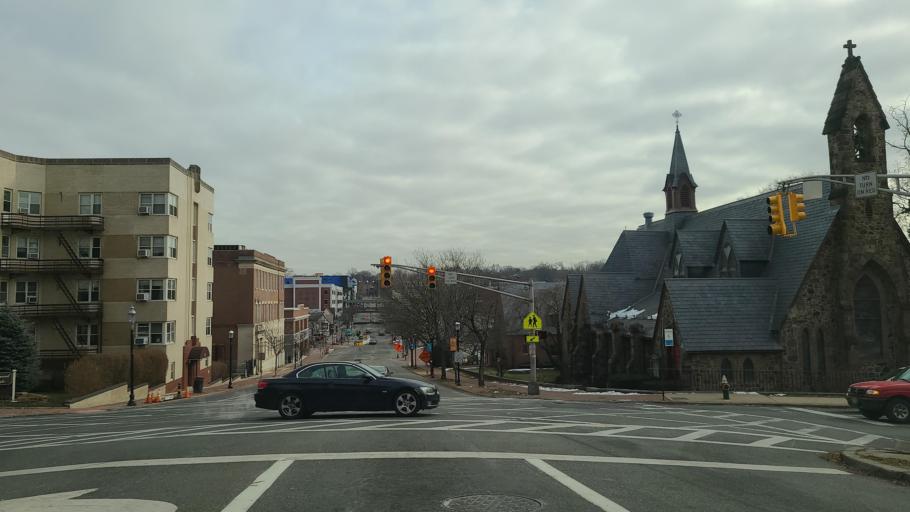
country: US
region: New Jersey
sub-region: Essex County
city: South Orange
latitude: 40.7476
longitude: -74.2637
